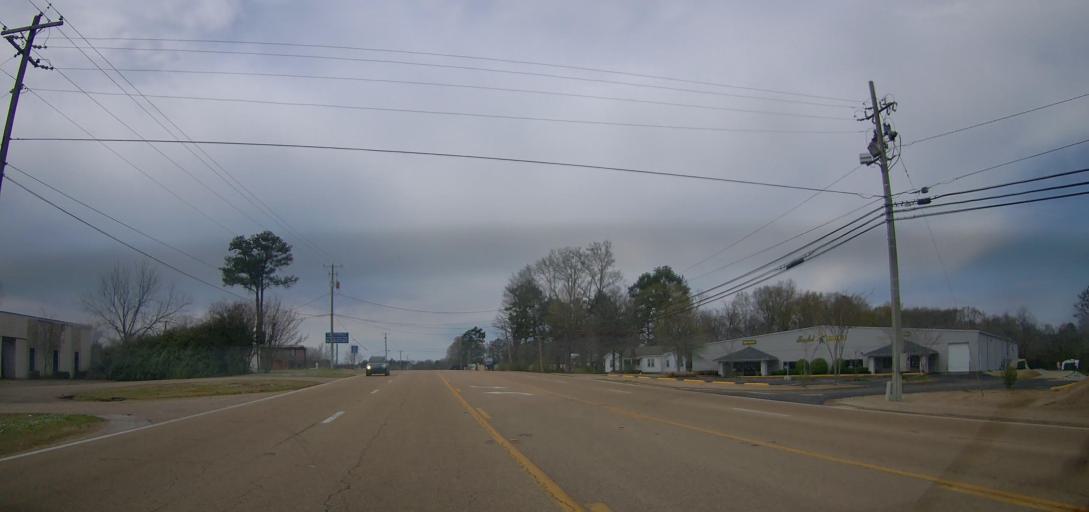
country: US
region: Mississippi
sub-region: Lee County
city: Tupelo
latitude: 34.2872
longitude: -88.7423
